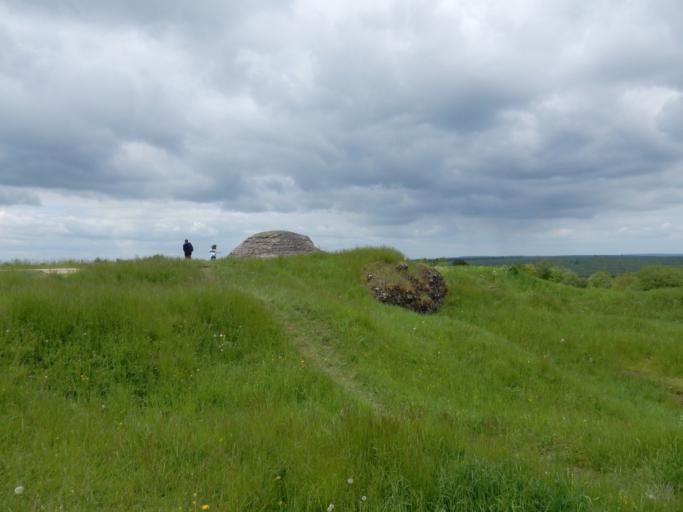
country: FR
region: Lorraine
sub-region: Departement de la Meuse
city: Verdun
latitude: 49.2171
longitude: 5.4396
